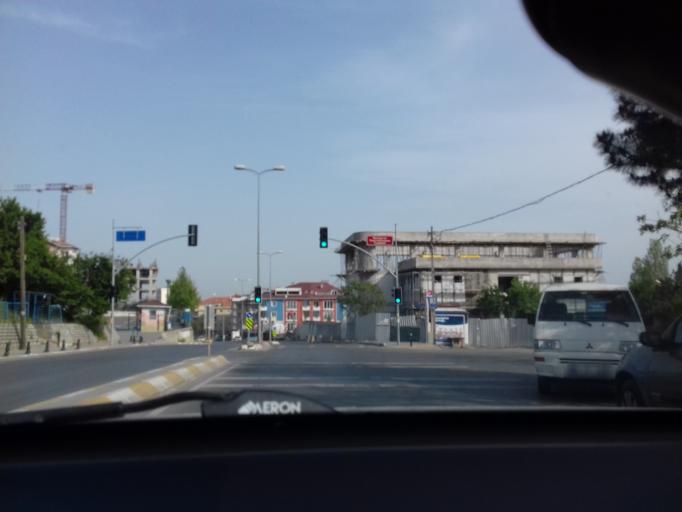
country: TR
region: Istanbul
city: Pendik
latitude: 40.9061
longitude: 29.2636
